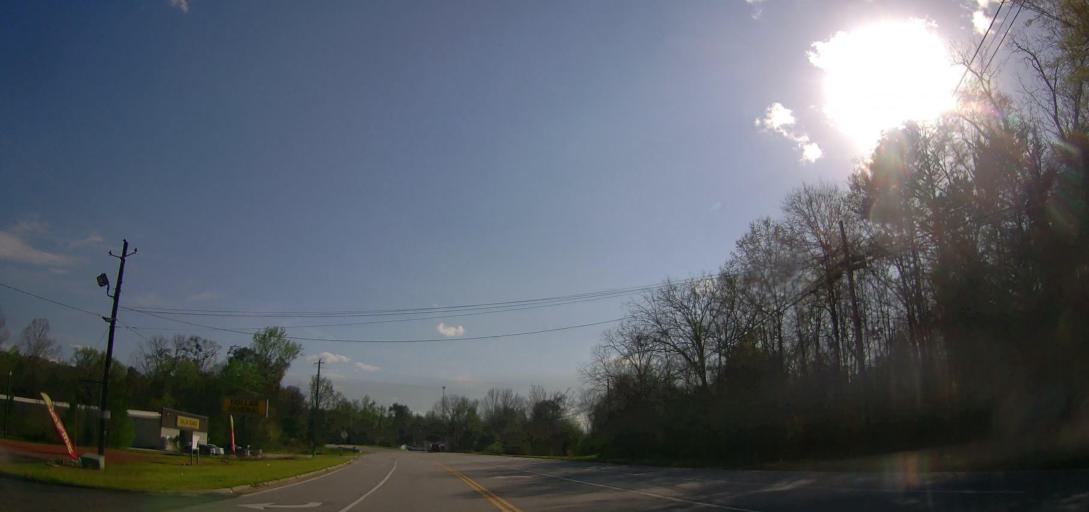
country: US
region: Georgia
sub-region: Baldwin County
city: Hardwick
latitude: 33.0391
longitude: -83.2349
